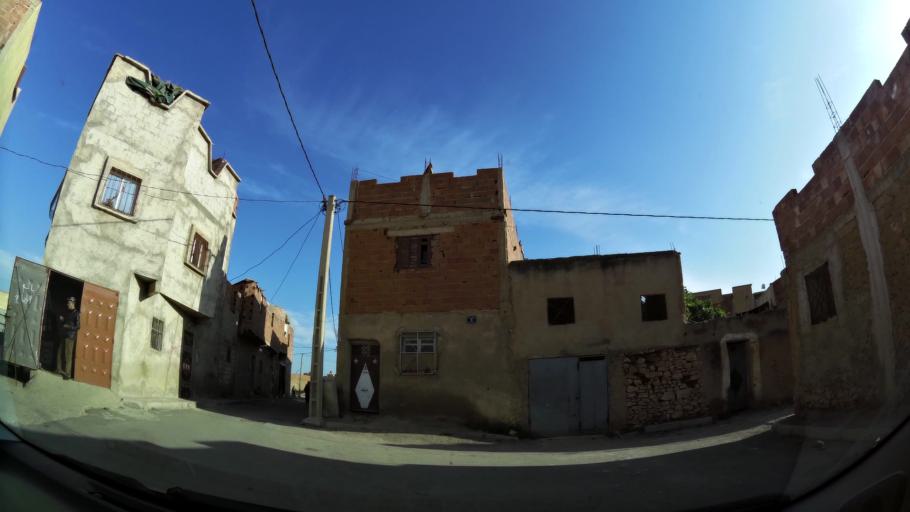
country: MA
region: Oriental
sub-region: Oujda-Angad
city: Oujda
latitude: 34.7154
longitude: -1.8972
